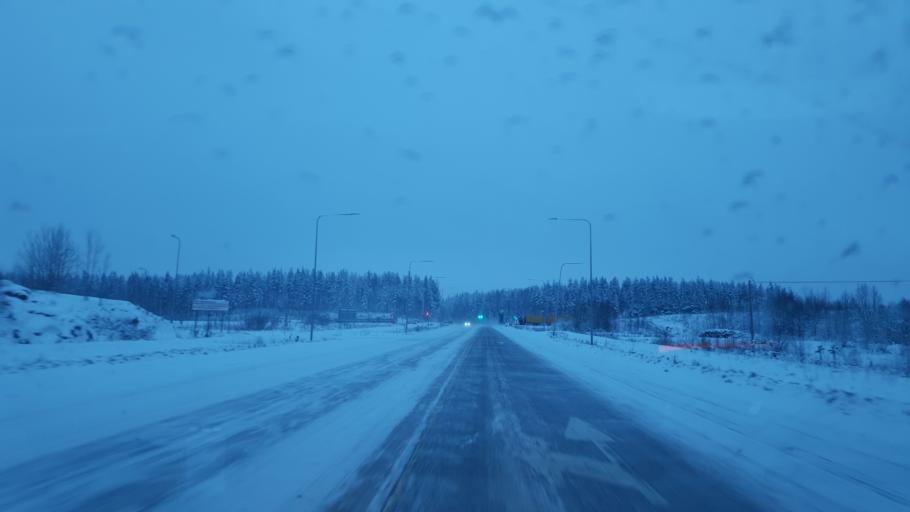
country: FI
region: Uusimaa
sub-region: Helsinki
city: Kerava
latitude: 60.3809
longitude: 25.1668
